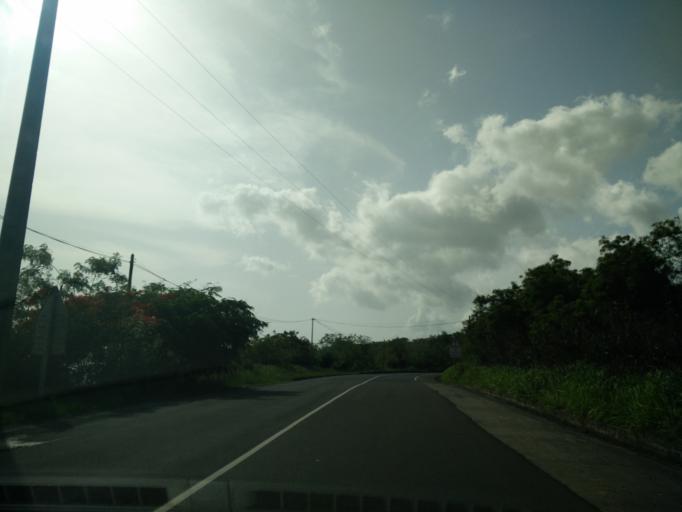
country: MQ
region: Martinique
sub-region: Martinique
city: Saint-Pierre
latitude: 14.7618
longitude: -61.1905
